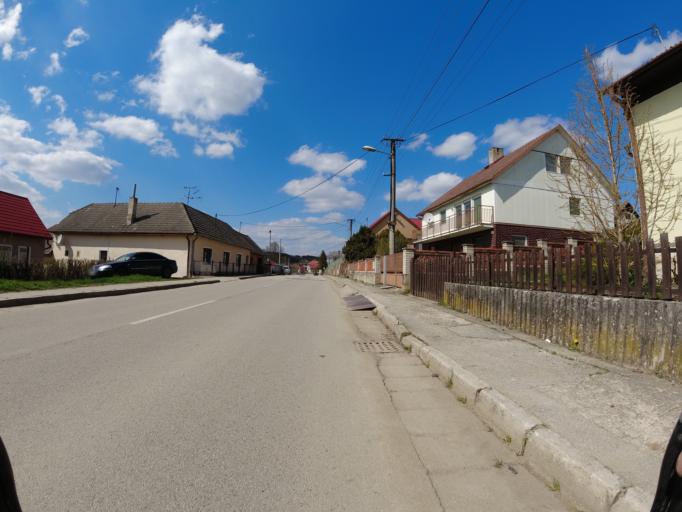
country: SK
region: Nitriansky
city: Stara Tura
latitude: 48.7392
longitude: 17.7247
